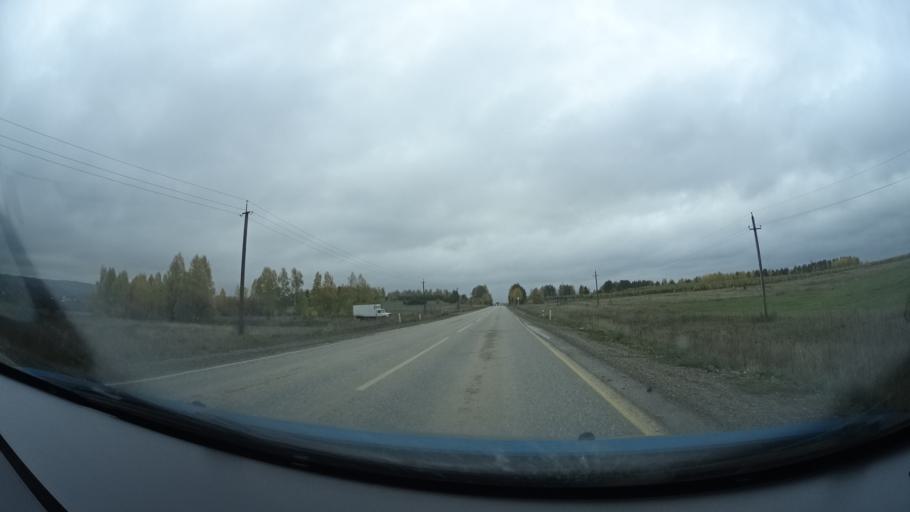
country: RU
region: Perm
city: Osa
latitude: 57.1670
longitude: 55.5315
